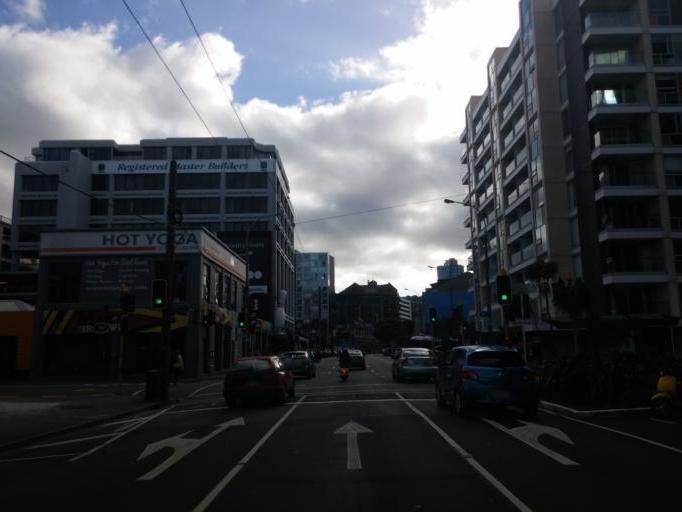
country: NZ
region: Wellington
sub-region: Wellington City
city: Wellington
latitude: -41.2923
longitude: 174.7822
